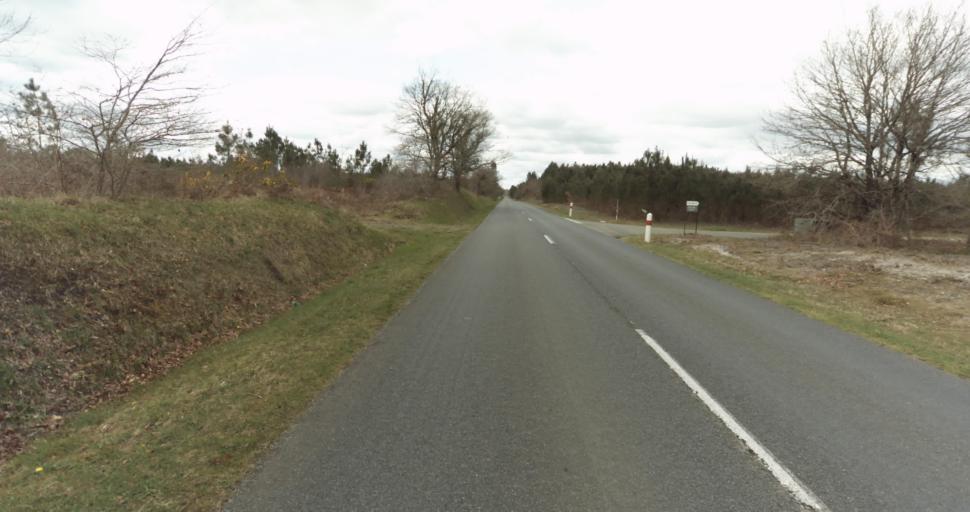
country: FR
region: Aquitaine
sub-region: Departement des Landes
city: Roquefort
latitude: 44.0577
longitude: -0.3912
